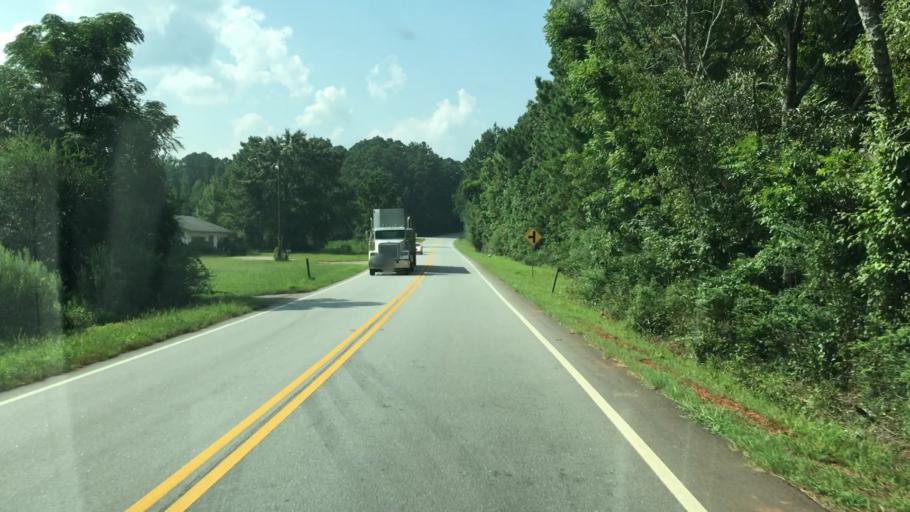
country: US
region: Georgia
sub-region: Jasper County
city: Monticello
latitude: 33.4072
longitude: -83.7589
